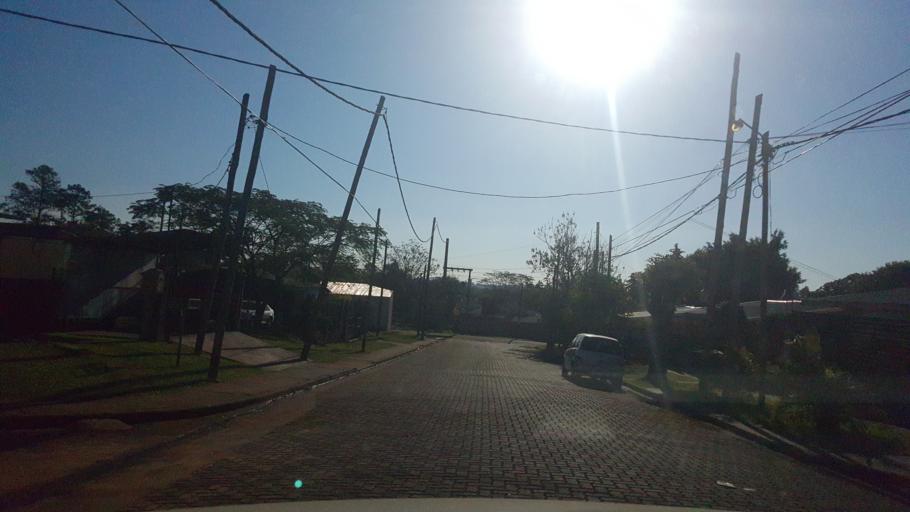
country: AR
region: Misiones
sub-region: Departamento de Capital
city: Posadas
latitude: -27.4062
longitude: -55.9369
